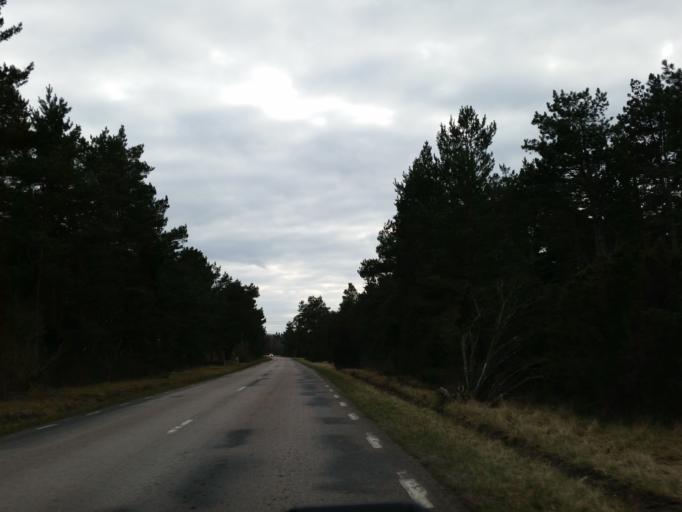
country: SE
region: Kalmar
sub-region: Morbylanga Kommun
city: Sodra Sandby
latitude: 56.5826
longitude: 16.6226
